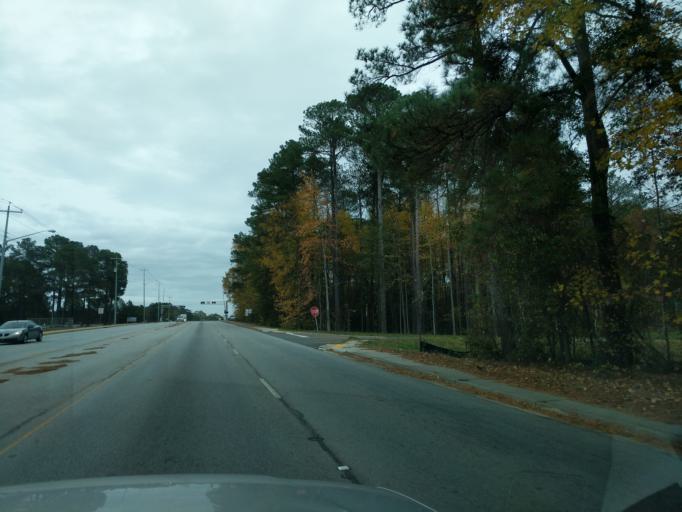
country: US
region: South Carolina
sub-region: Newberry County
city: Newberry
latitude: 34.2957
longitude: -81.6266
